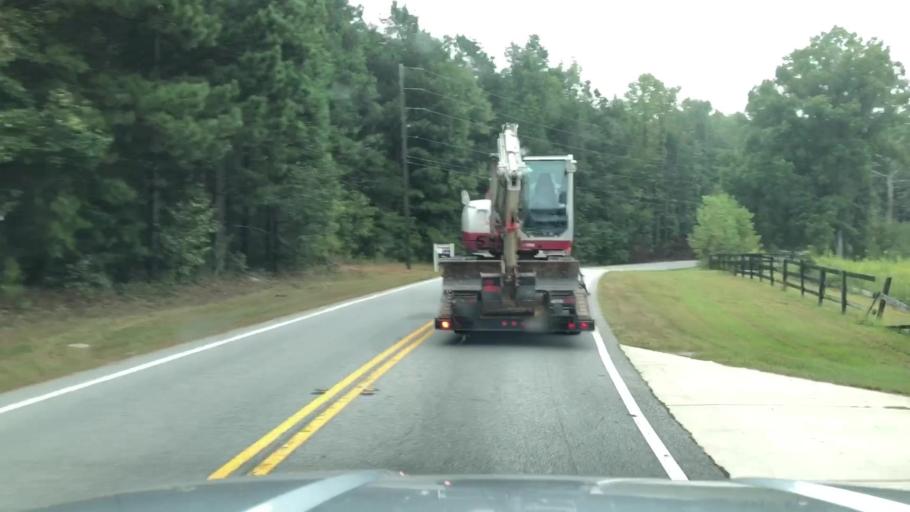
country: US
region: Georgia
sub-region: Bartow County
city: Emerson
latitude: 34.0593
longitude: -84.8018
